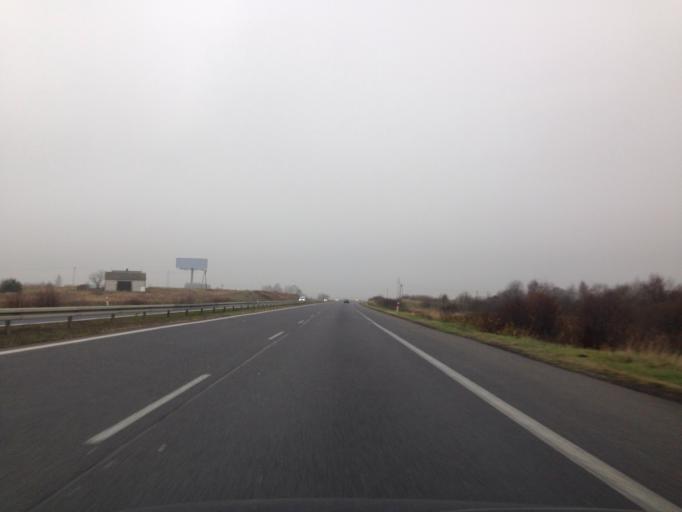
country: PL
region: Lodz Voivodeship
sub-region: Powiat radomszczanski
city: Kamiensk
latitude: 51.2274
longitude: 19.5077
